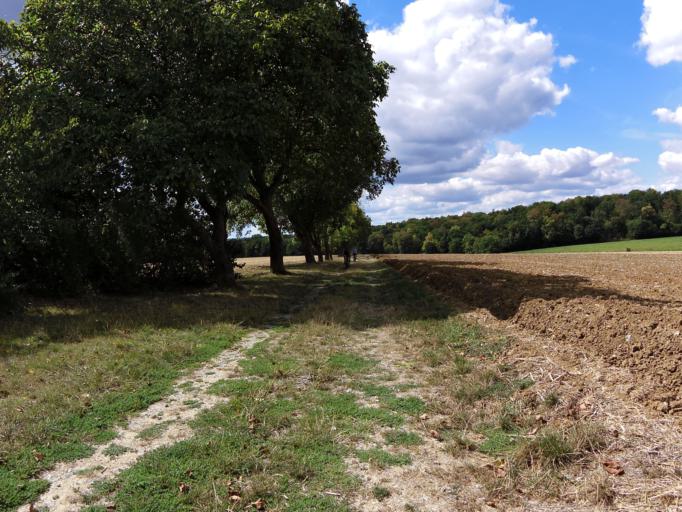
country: DE
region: Bavaria
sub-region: Regierungsbezirk Unterfranken
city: Gadheim
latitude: 49.8466
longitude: 9.9011
